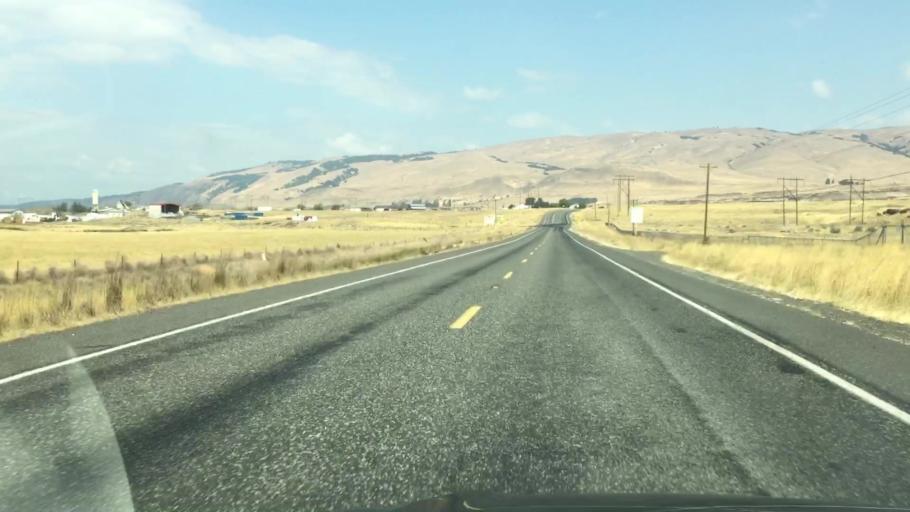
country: US
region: Washington
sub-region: Klickitat County
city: Dallesport
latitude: 45.6293
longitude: -121.1504
